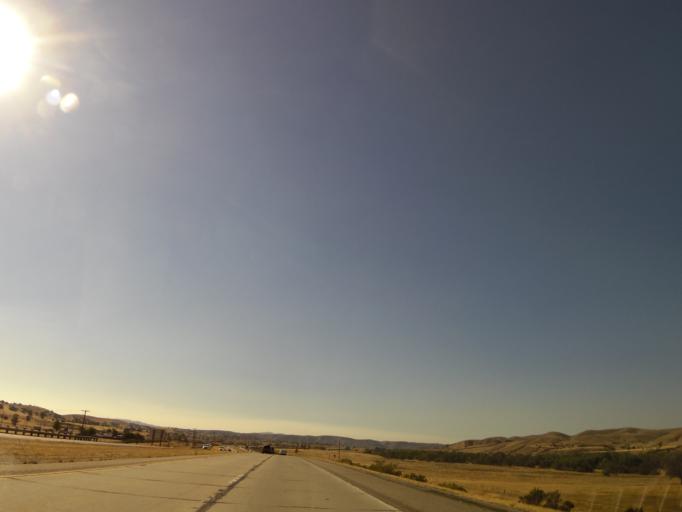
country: US
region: California
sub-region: San Luis Obispo County
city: San Miguel
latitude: 35.7759
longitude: -120.7132
